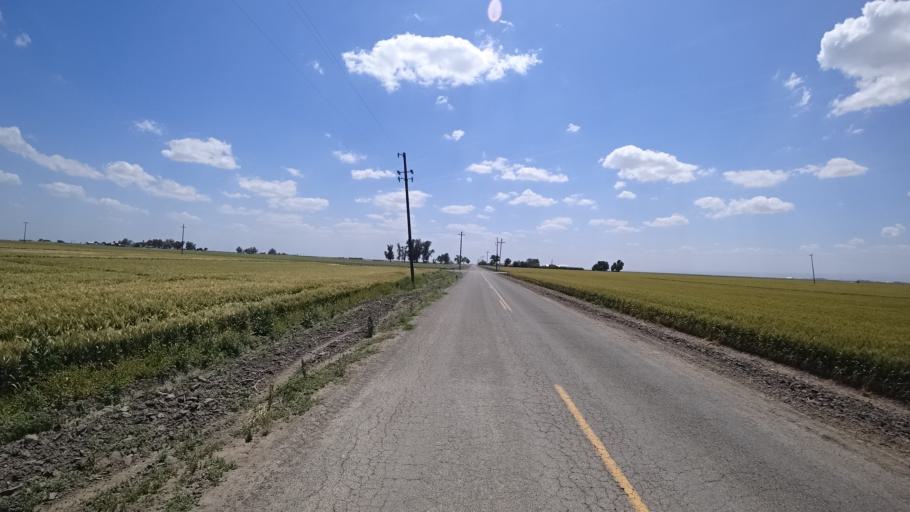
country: US
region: California
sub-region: Kings County
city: Stratford
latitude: 36.1683
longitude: -119.8250
